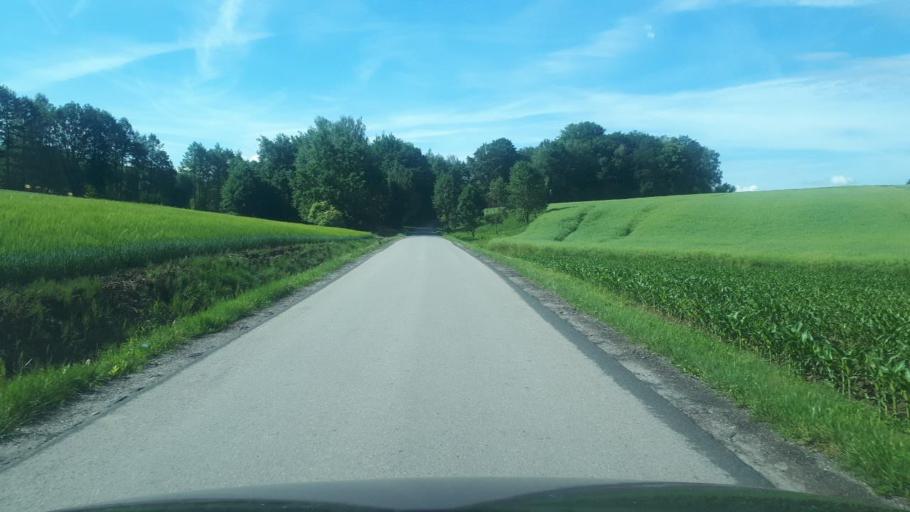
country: PL
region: Silesian Voivodeship
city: Janowice
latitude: 49.8992
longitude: 19.1094
